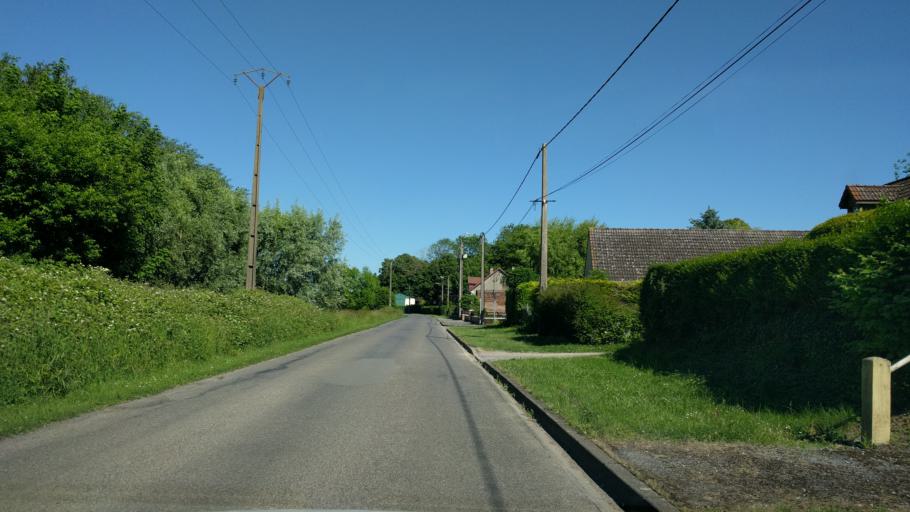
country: FR
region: Picardie
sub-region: Departement de la Somme
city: Peronne
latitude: 49.9199
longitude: 2.9230
